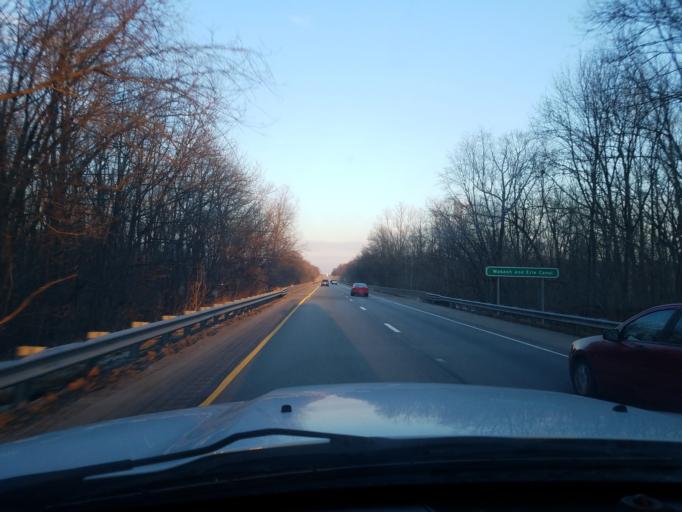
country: US
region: Indiana
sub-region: Warrick County
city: Chandler
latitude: 38.1738
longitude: -87.4177
